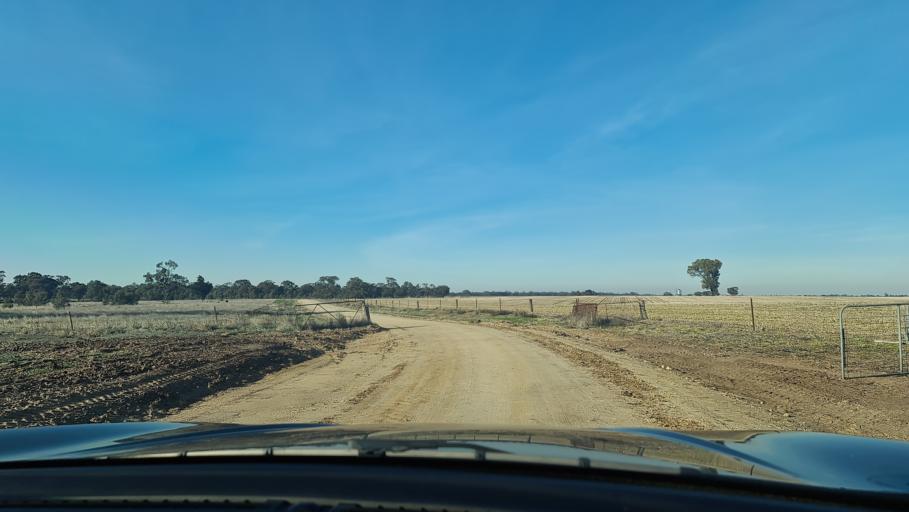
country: AU
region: Victoria
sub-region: Horsham
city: Horsham
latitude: -36.3540
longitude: 142.3945
